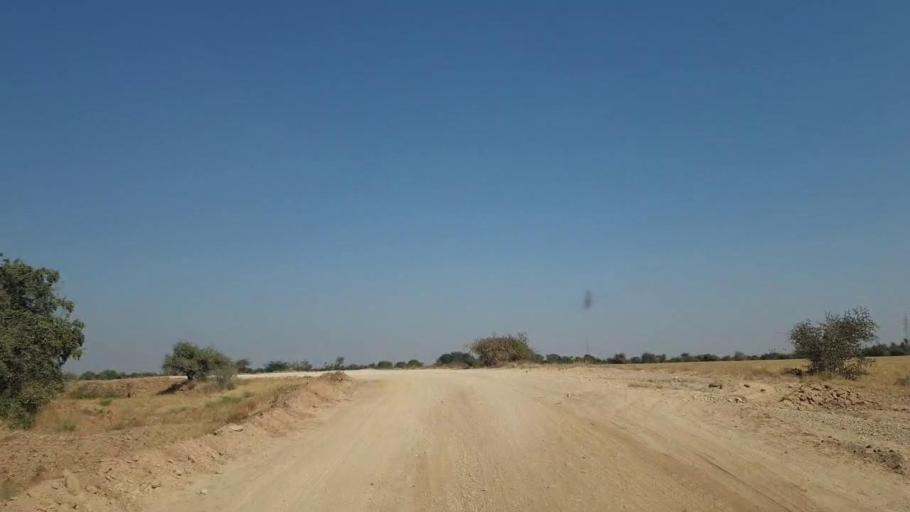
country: PK
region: Sindh
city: Jamshoro
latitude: 25.2666
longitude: 67.8050
